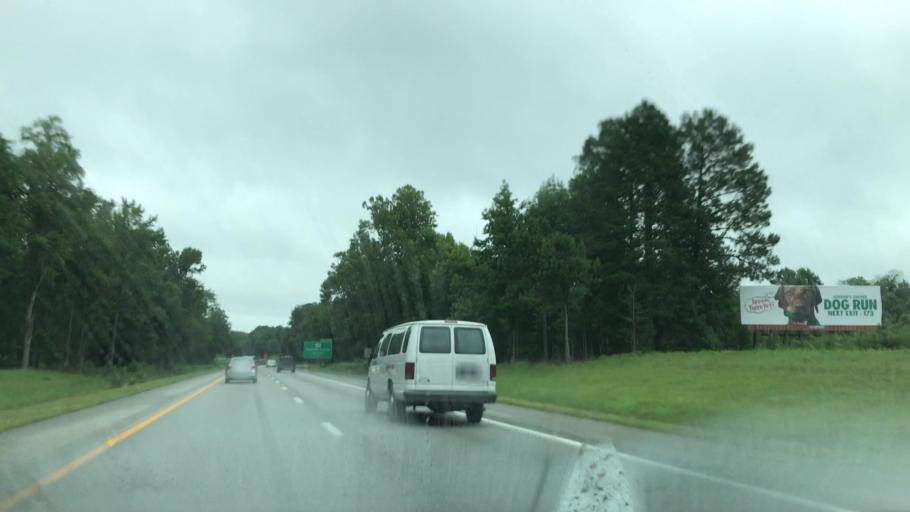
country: US
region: North Carolina
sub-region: Halifax County
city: Weldon
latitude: 36.4114
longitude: -77.6381
